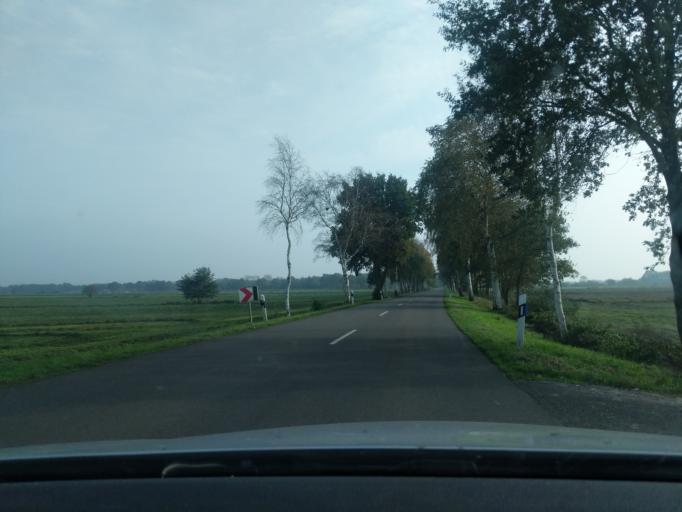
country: DE
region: Lower Saxony
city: Stinstedt
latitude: 53.6523
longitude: 8.9879
